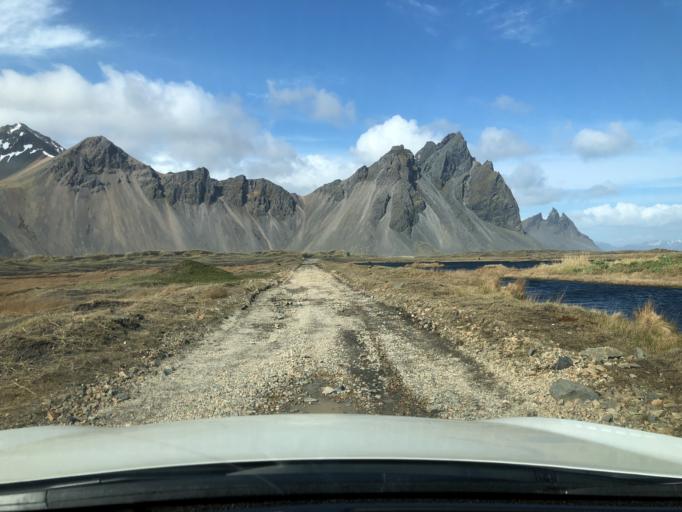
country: IS
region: East
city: Hoefn
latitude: 64.2420
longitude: -14.9717
